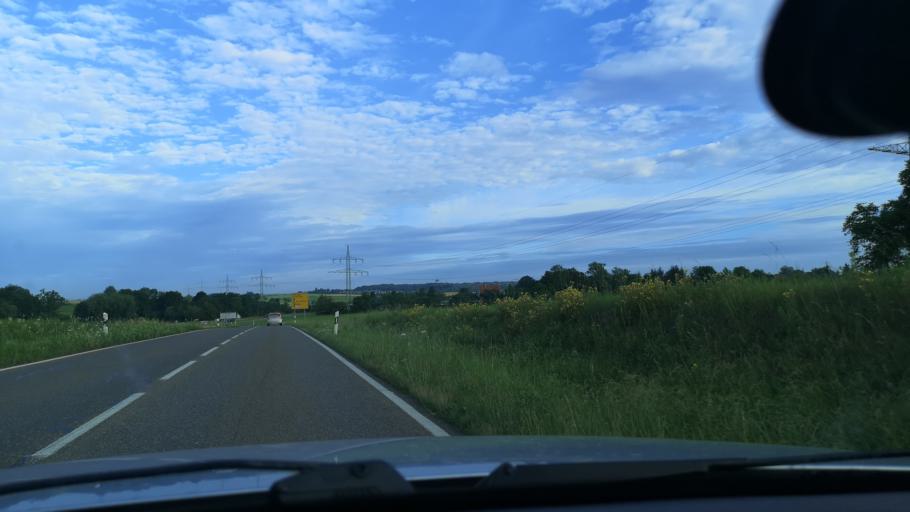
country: DE
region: Baden-Wuerttemberg
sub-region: Regierungsbezirk Stuttgart
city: Eschenbach
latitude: 48.6684
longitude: 9.6866
